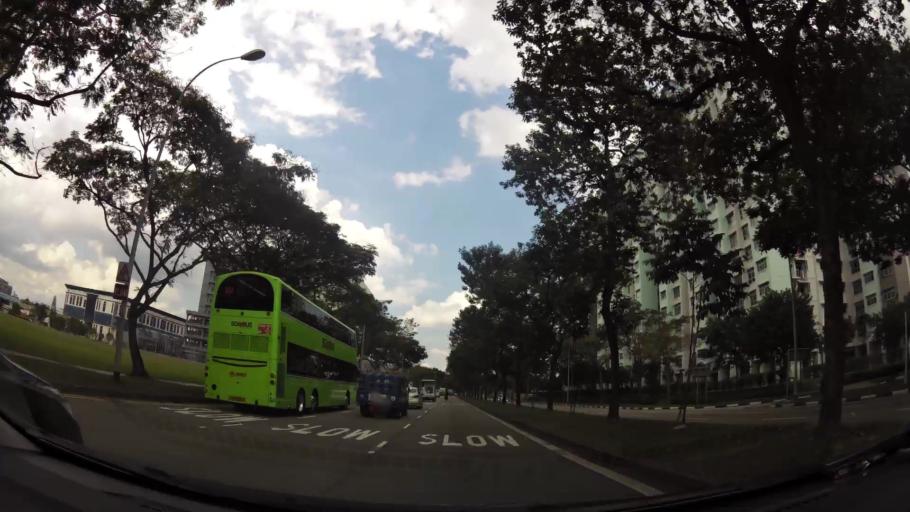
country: MY
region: Johor
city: Johor Bahru
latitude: 1.4492
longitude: 103.8004
